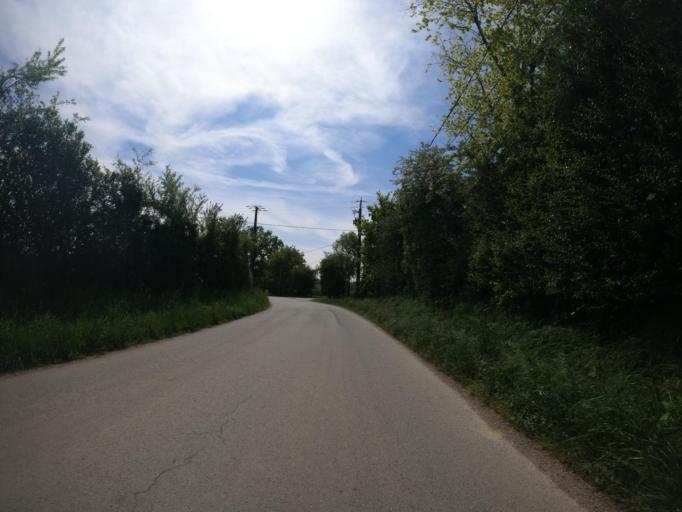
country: FR
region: Poitou-Charentes
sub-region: Departement des Deux-Sevres
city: La Chapelle-Saint-Laurent
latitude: 46.6669
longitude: -0.5067
